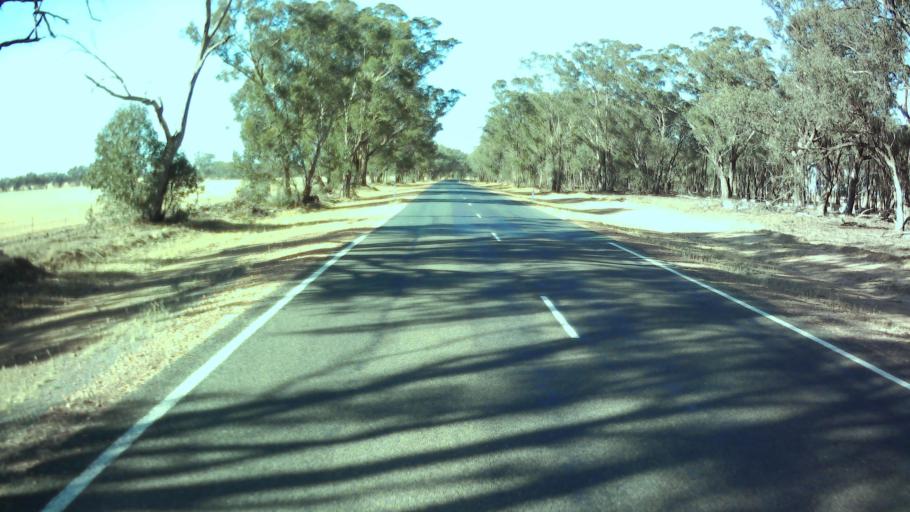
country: AU
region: New South Wales
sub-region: Weddin
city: Grenfell
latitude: -34.0054
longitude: 148.1238
